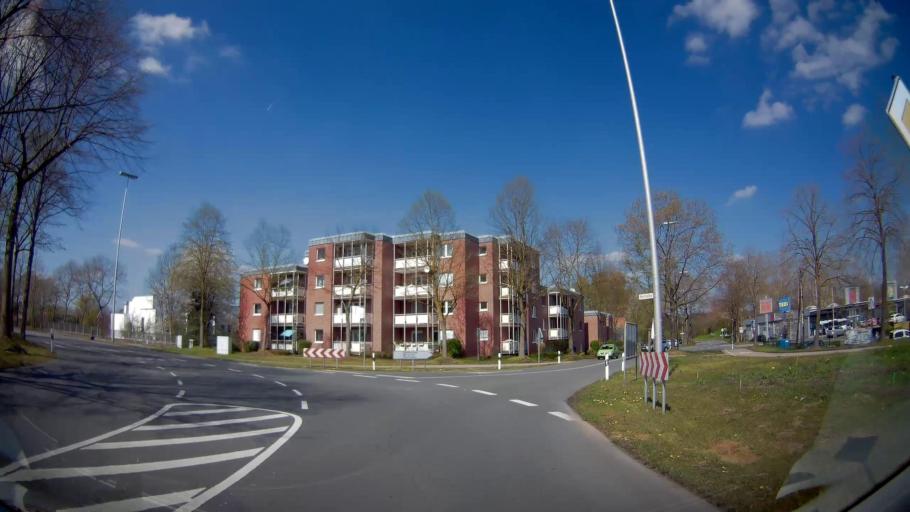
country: DE
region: North Rhine-Westphalia
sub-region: Regierungsbezirk Munster
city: Klein Reken
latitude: 51.7257
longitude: 7.0257
